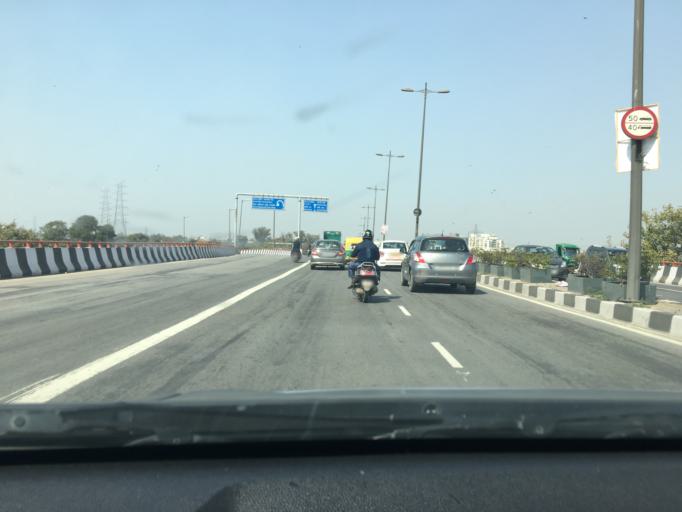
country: IN
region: NCT
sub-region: North Delhi
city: Delhi
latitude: 28.6434
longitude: 77.2690
